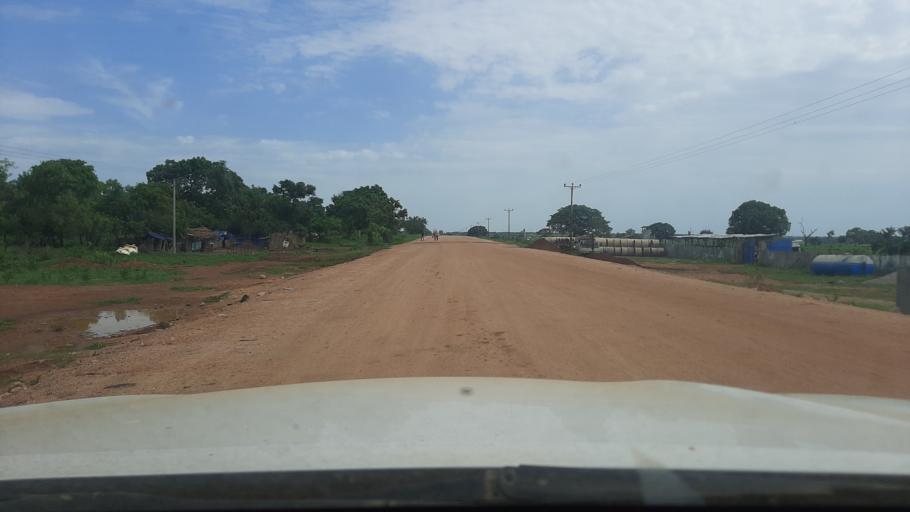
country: ET
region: Gambela
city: Gambela
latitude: 8.0324
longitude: 34.5769
